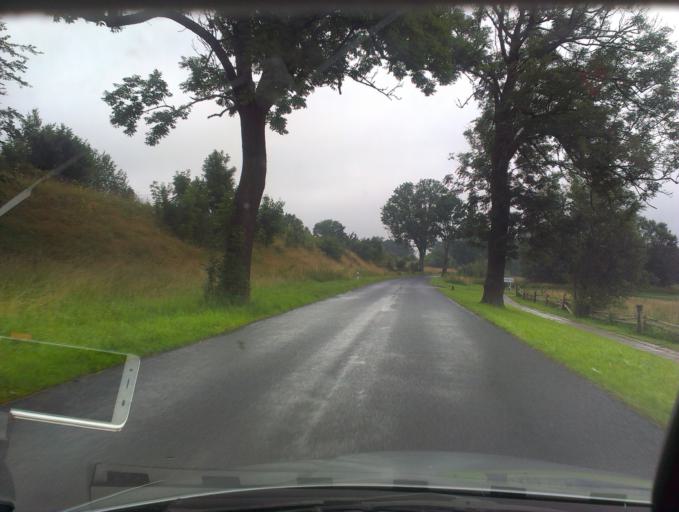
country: PL
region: West Pomeranian Voivodeship
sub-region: Powiat szczecinecki
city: Barwice
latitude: 53.7549
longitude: 16.3639
